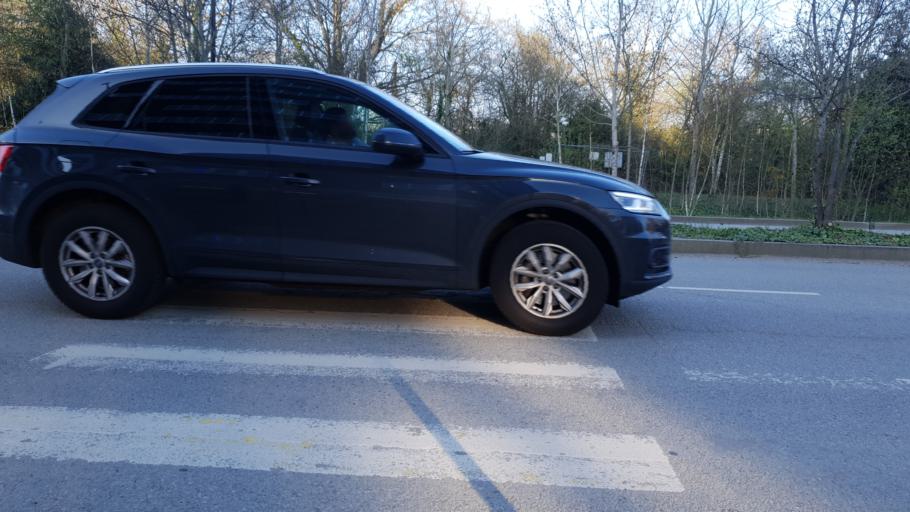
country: FR
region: Brittany
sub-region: Departement d'Ille-et-Vilaine
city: Saint-Jacques-de-la-Lande
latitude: 48.0933
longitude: -1.7041
